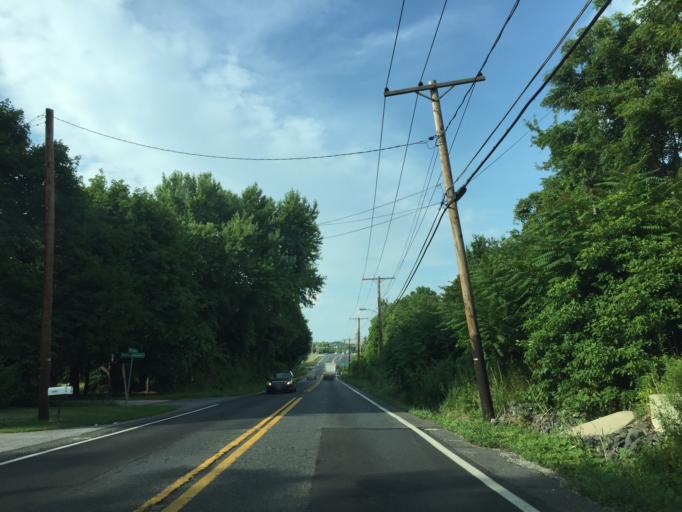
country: US
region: Maryland
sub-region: Baltimore County
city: White Marsh
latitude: 39.3637
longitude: -76.4515
